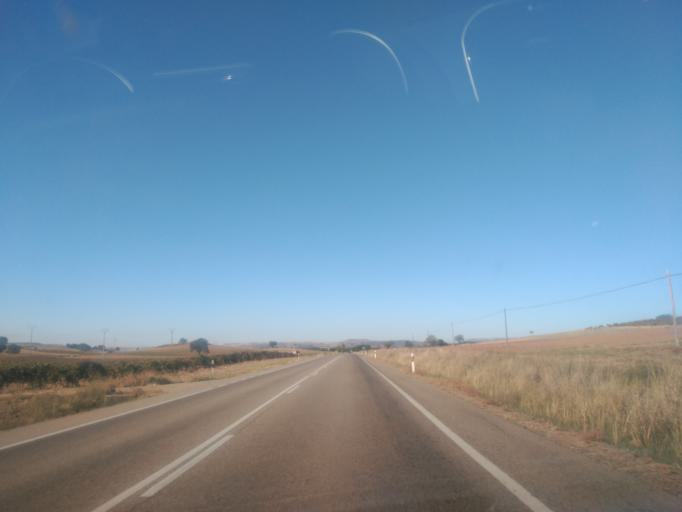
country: ES
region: Castille and Leon
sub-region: Provincia de Burgos
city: Fuentelisendo
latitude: 41.6175
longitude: -3.9088
